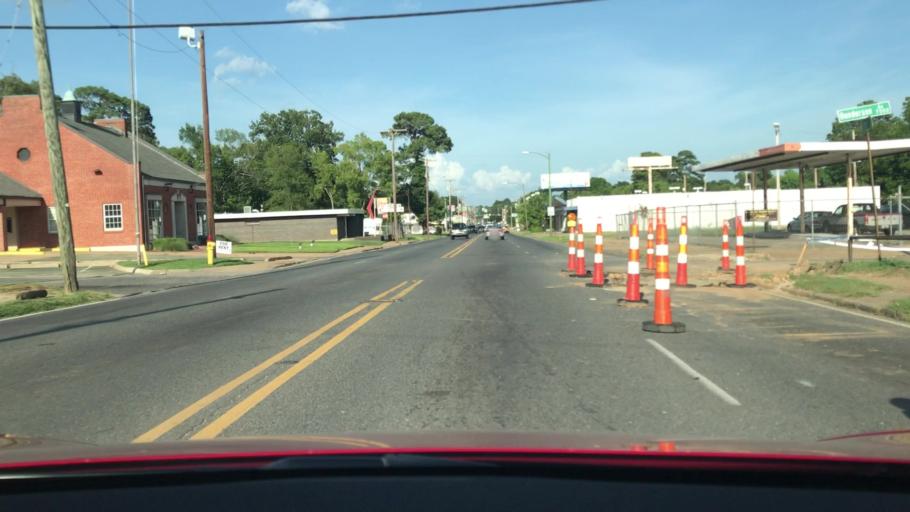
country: US
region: Louisiana
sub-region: Bossier Parish
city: Bossier City
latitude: 32.4420
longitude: -93.7526
